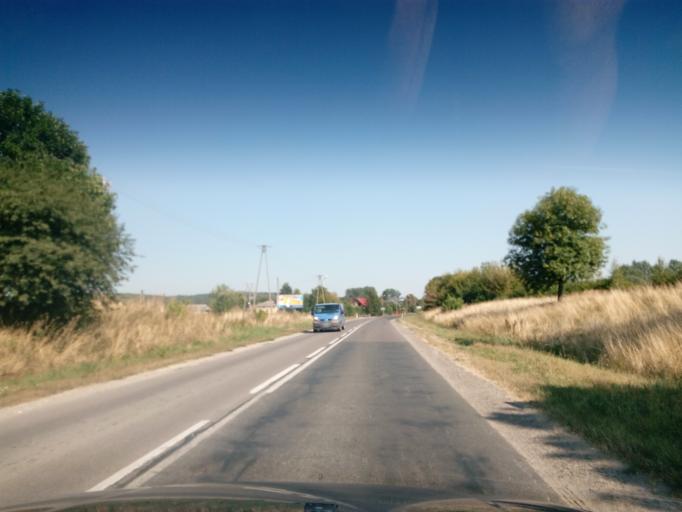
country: PL
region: Lublin Voivodeship
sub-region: Powiat hrubieszowski
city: Horodlo
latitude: 50.8424
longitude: 24.0055
